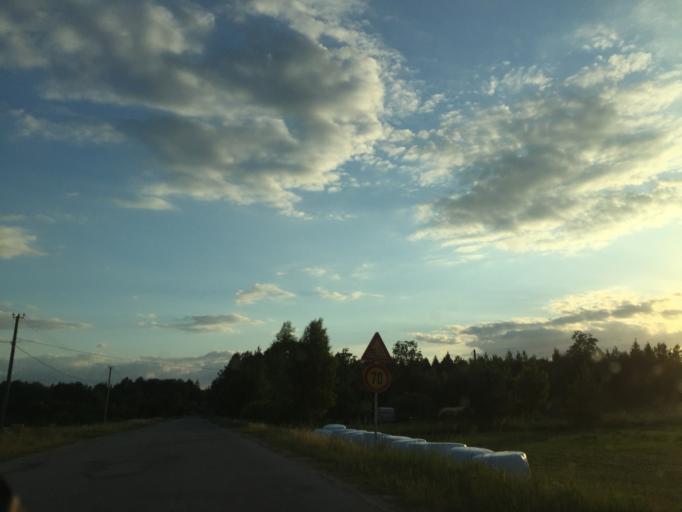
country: LV
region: Sigulda
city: Sigulda
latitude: 57.1086
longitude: 24.9314
